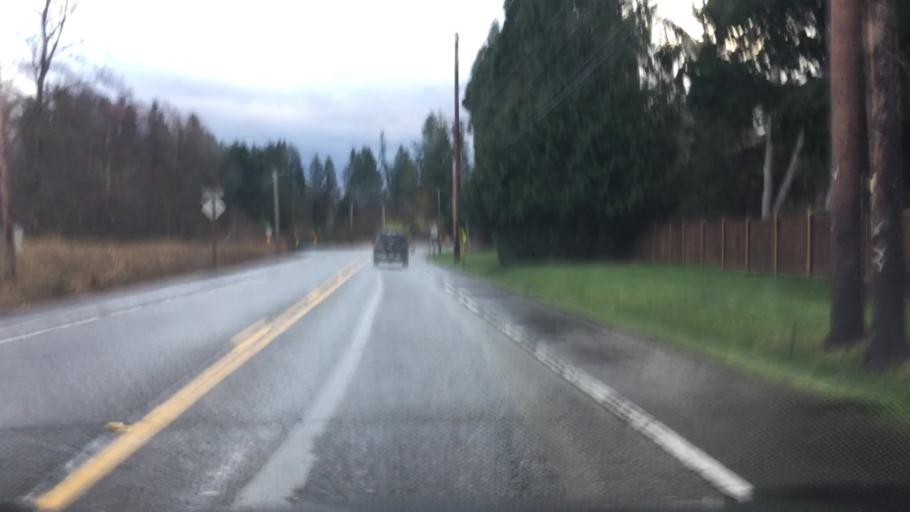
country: US
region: Washington
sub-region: King County
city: Cottage Lake
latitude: 47.7396
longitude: -122.0803
